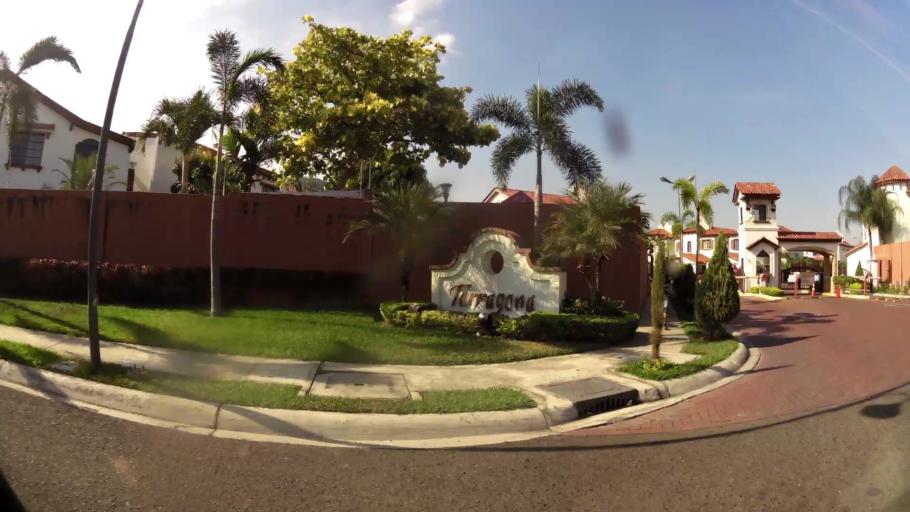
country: EC
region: Guayas
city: Santa Lucia
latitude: -2.1854
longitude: -79.9965
